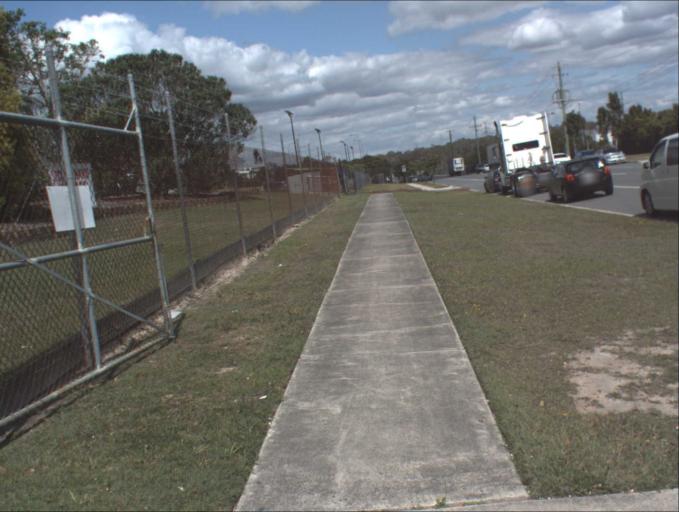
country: AU
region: Queensland
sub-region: Logan
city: Logan Reserve
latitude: -27.6843
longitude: 153.0704
